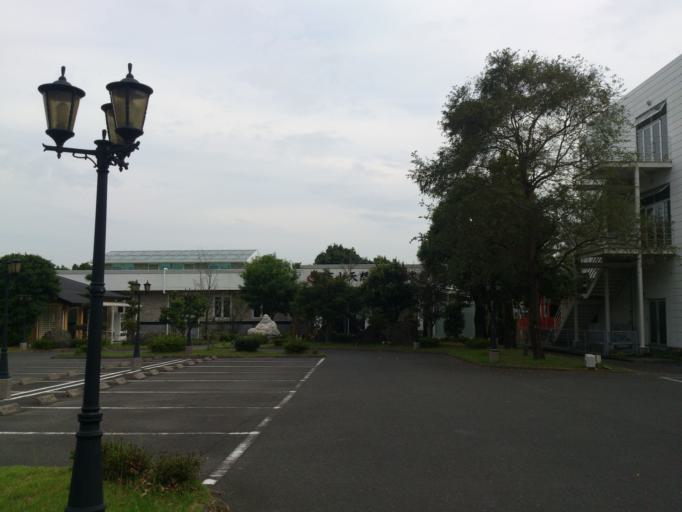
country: JP
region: Kagoshima
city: Kanoya
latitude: 31.3518
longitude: 130.9465
